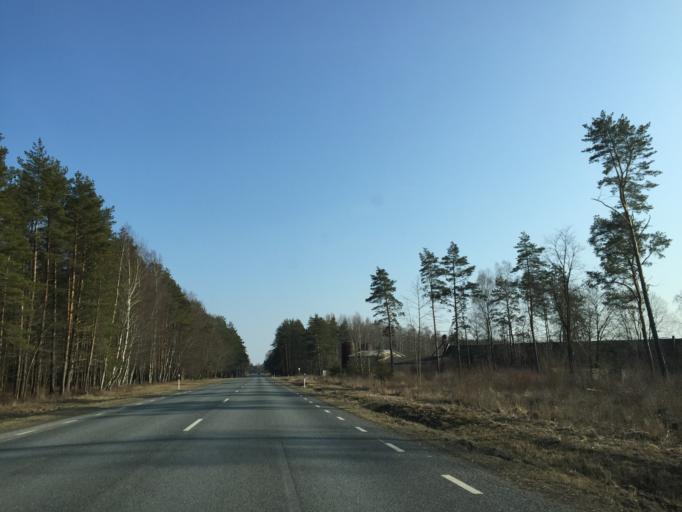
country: EE
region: Saare
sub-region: Orissaare vald
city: Orissaare
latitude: 58.5980
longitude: 23.3227
